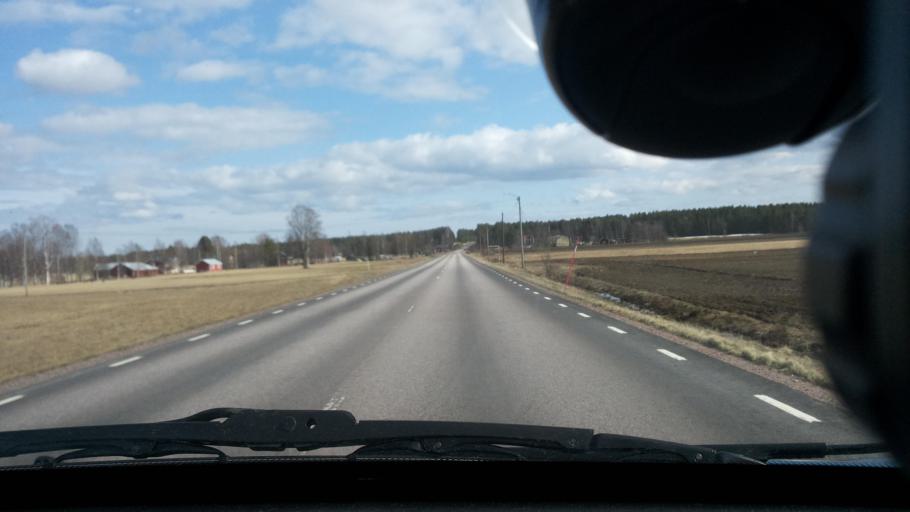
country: SE
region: Norrbotten
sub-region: Lulea Kommun
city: Sodra Sunderbyn
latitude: 65.6413
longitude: 21.8980
